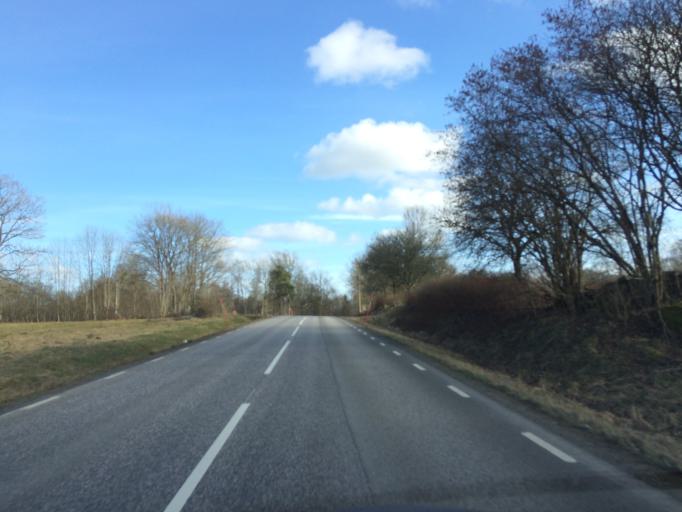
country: SE
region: Kronoberg
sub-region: Almhults Kommun
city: AElmhult
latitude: 56.5746
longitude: 14.1116
